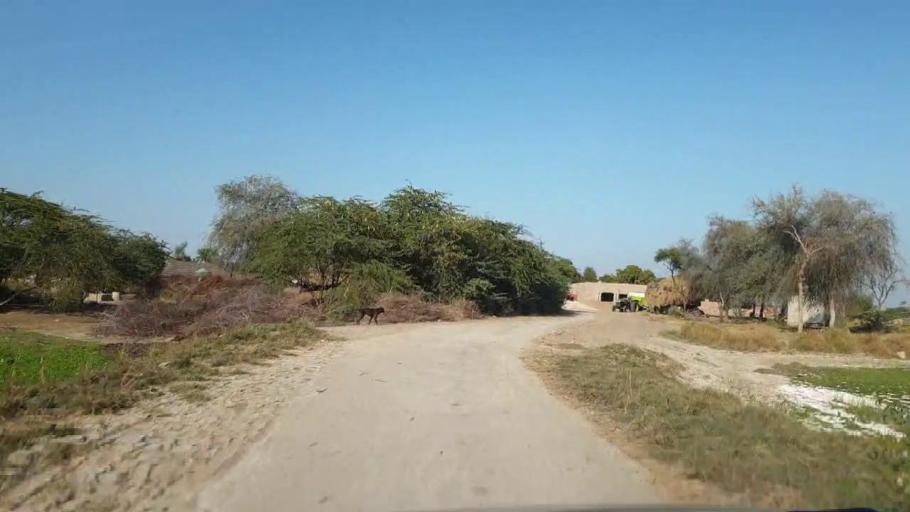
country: PK
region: Sindh
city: Khadro
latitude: 26.1912
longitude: 68.7658
